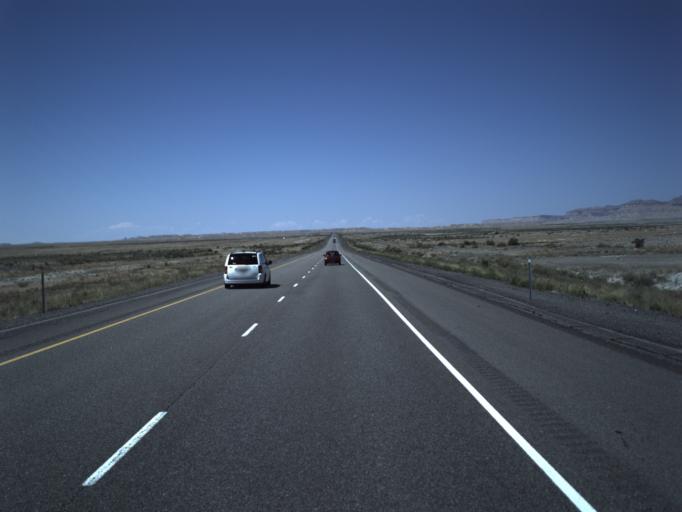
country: US
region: Utah
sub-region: Grand County
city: Moab
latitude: 38.9427
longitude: -109.5523
